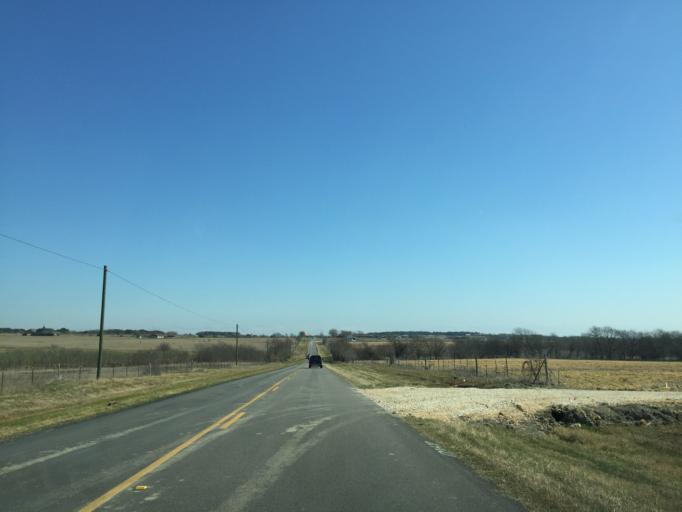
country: US
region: Texas
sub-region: Williamson County
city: Serenada
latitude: 30.7339
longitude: -97.6099
